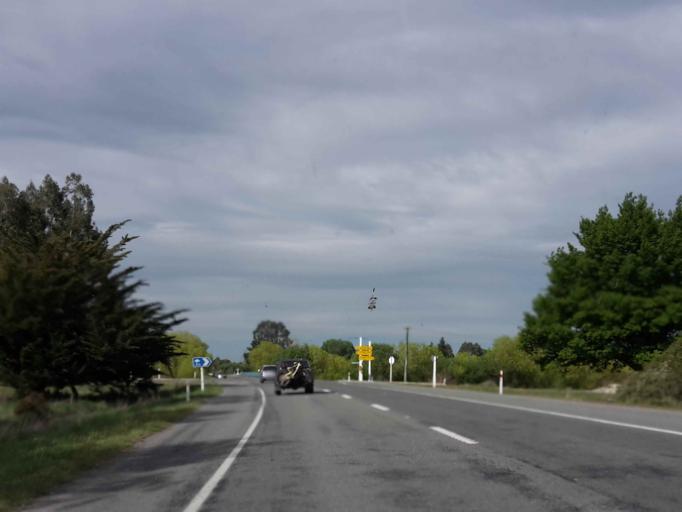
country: NZ
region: Canterbury
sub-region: Timaru District
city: Pleasant Point
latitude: -44.1175
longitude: 171.2068
